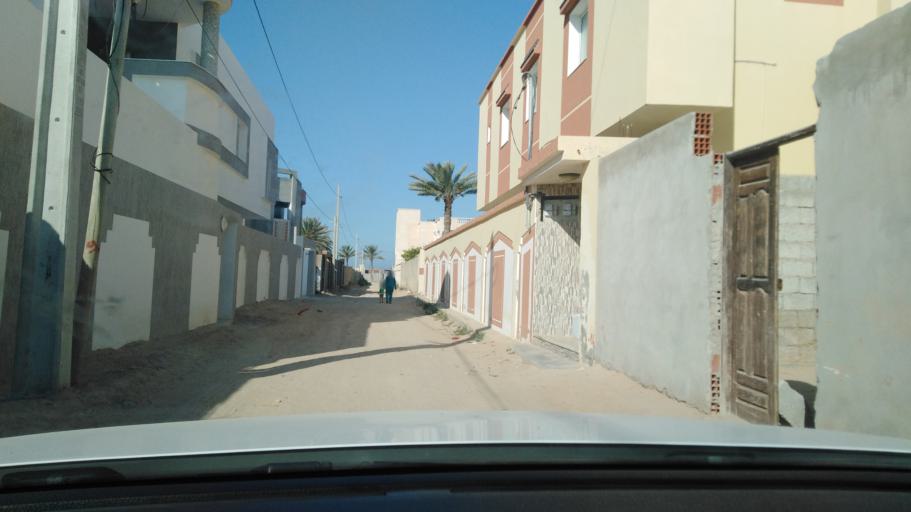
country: TN
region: Qabis
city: Gabes
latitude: 33.9414
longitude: 10.0722
